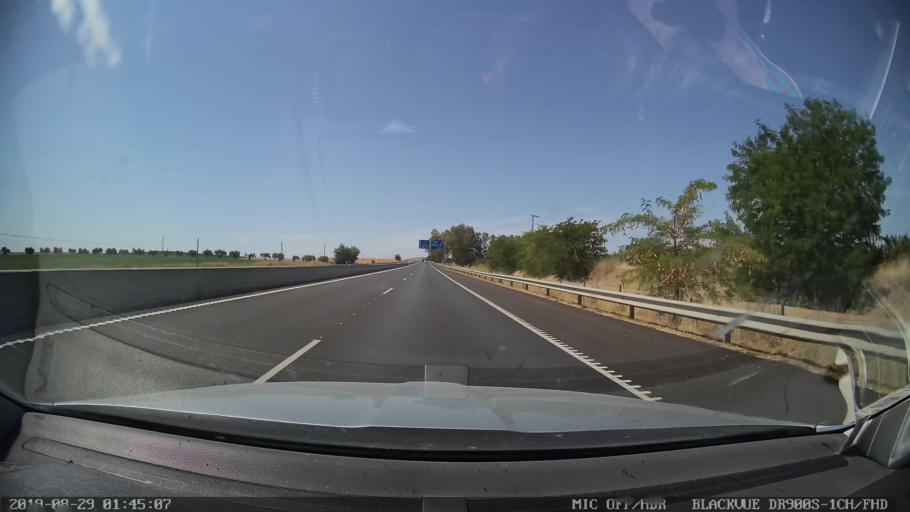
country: PT
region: Portalegre
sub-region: Elvas
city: Elvas
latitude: 38.8881
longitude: -7.0914
